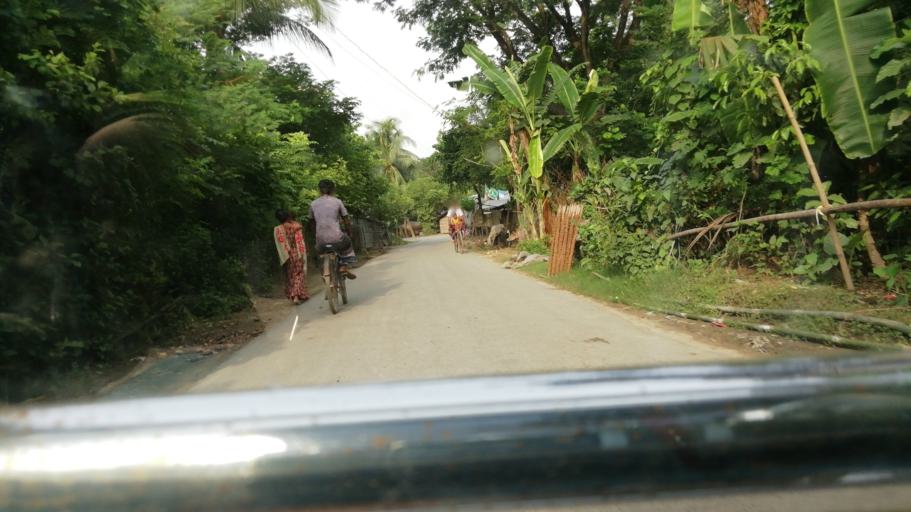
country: BD
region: Khulna
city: Kesabpur
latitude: 23.0319
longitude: 89.2774
